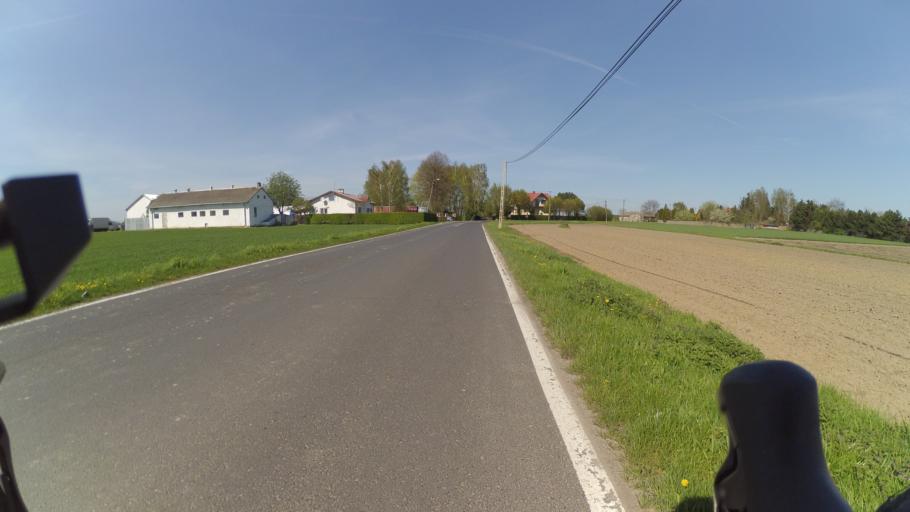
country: PL
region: Masovian Voivodeship
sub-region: Powiat warszawski zachodni
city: Leszno
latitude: 52.2453
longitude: 20.5495
